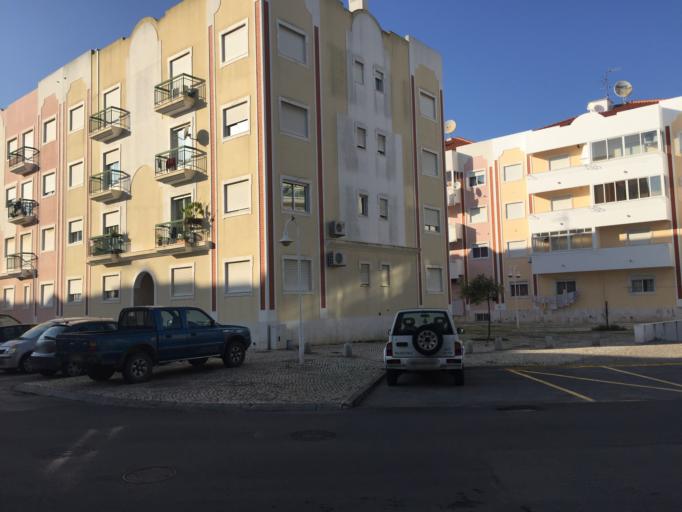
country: PT
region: Faro
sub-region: Vila Real de Santo Antonio
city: Vila Real de Santo Antonio
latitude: 37.1929
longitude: -7.4196
